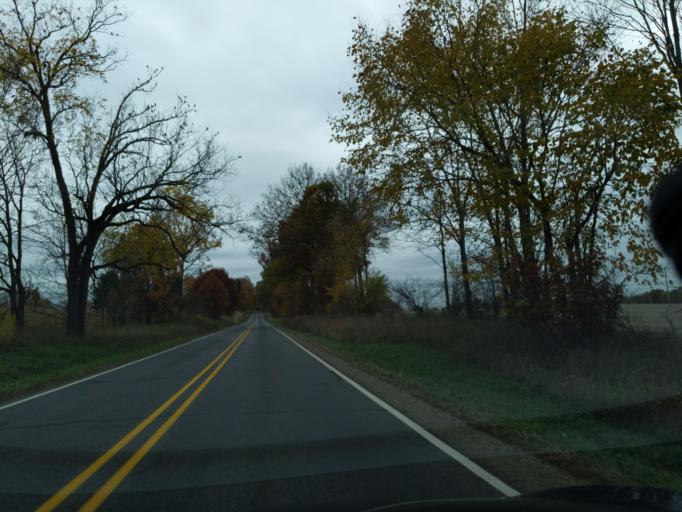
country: US
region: Michigan
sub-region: Jackson County
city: Spring Arbor
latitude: 42.3490
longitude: -84.6005
